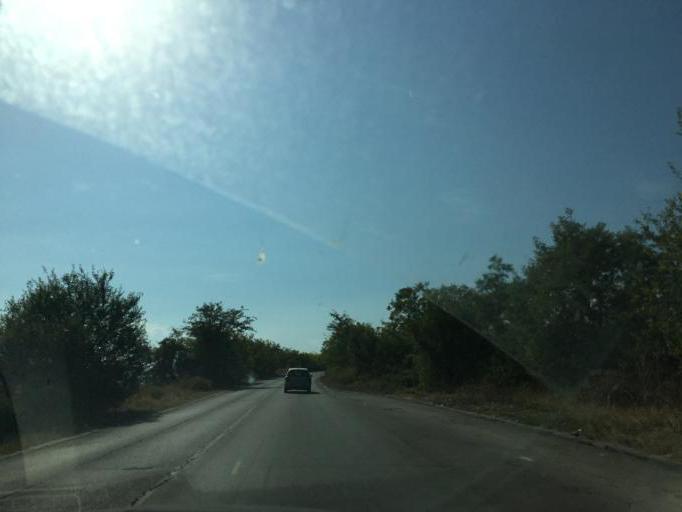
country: BG
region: Pazardzhik
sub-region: Obshtina Peshtera
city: Peshtera
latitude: 42.1071
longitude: 24.2977
